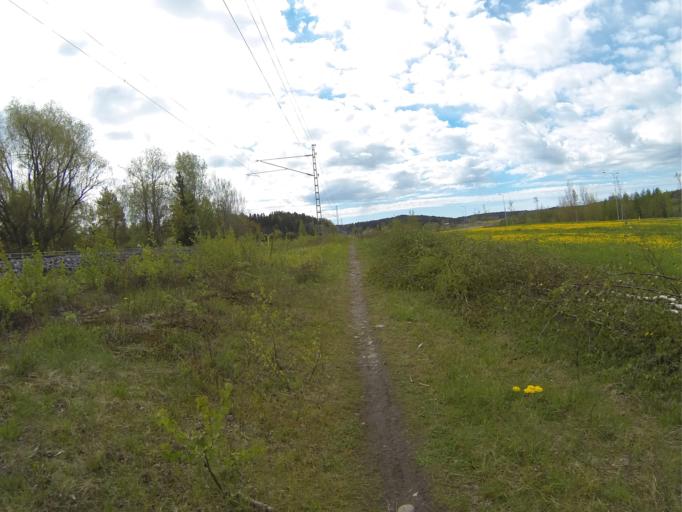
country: FI
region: Varsinais-Suomi
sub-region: Salo
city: Salo
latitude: 60.3685
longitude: 23.1190
